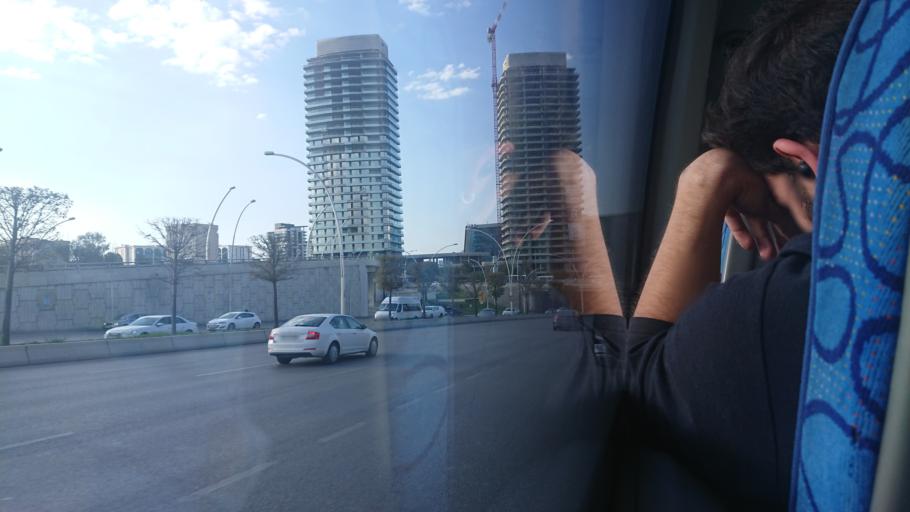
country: TR
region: Ankara
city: Ankara
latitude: 39.9070
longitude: 32.7870
